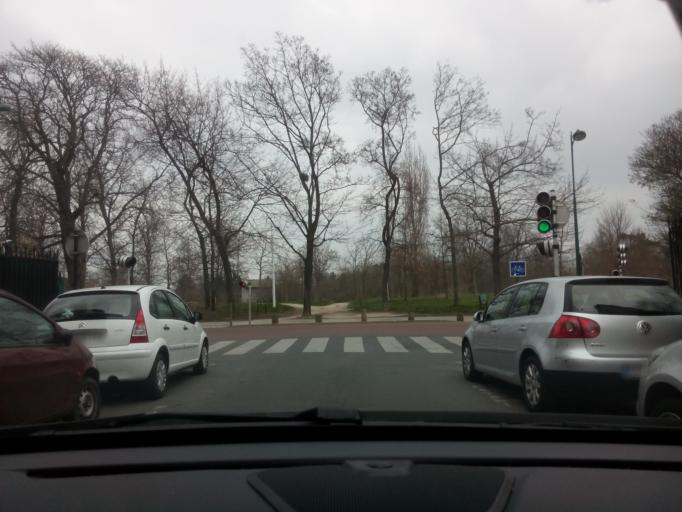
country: FR
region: Ile-de-France
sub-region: Departement du Val-de-Marne
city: Charenton-le-Pont
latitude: 48.8262
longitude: 2.4073
